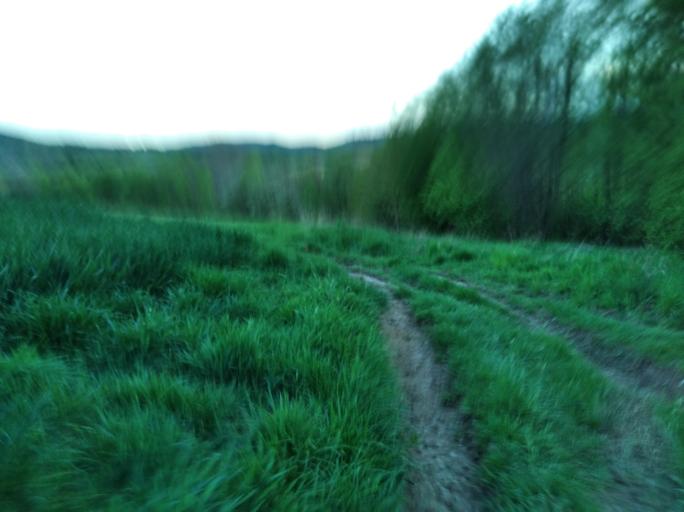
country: PL
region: Subcarpathian Voivodeship
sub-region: Powiat strzyzowski
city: Wysoka Strzyzowska
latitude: 49.8546
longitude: 21.7634
